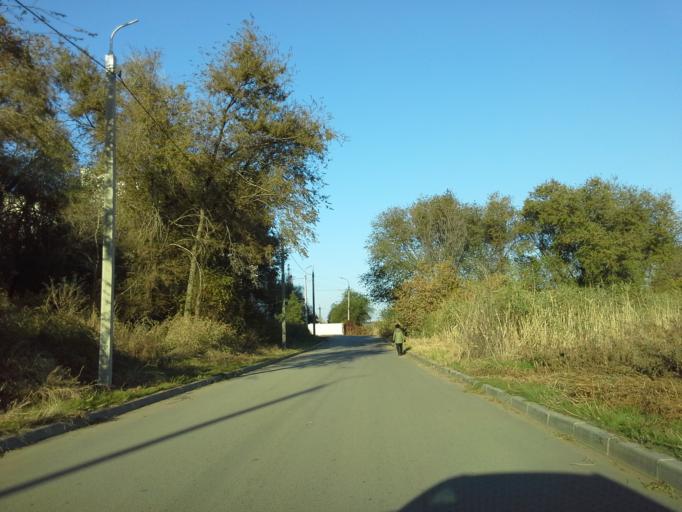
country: RU
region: Volgograd
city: Vodstroy
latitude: 48.8213
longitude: 44.6431
